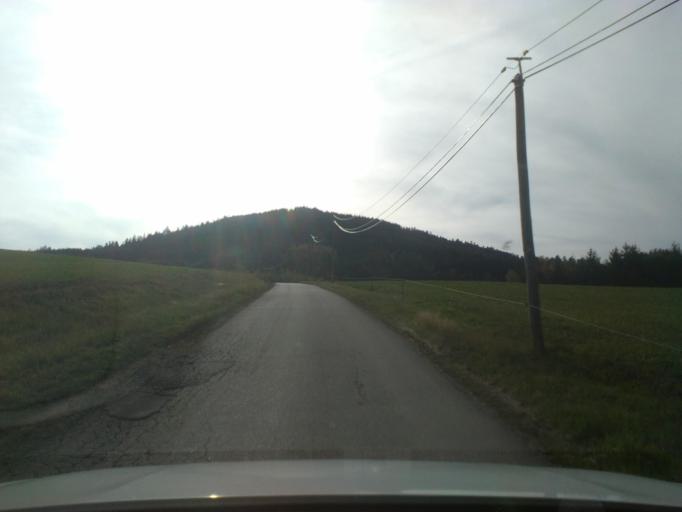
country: FR
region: Lorraine
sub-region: Departement des Vosges
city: Senones
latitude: 48.3862
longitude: 7.0022
